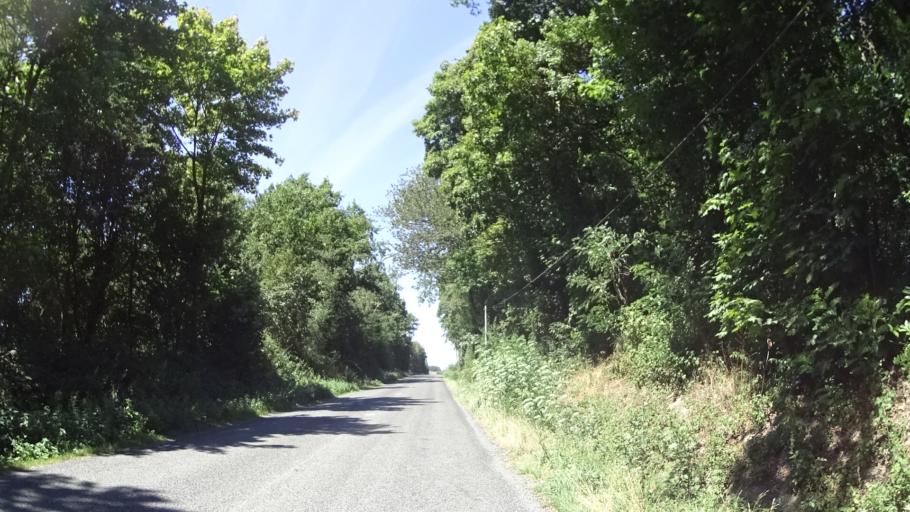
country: FR
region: Pays de la Loire
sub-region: Departement de Maine-et-Loire
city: Grez-Neuville
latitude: 47.6283
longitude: -0.7441
